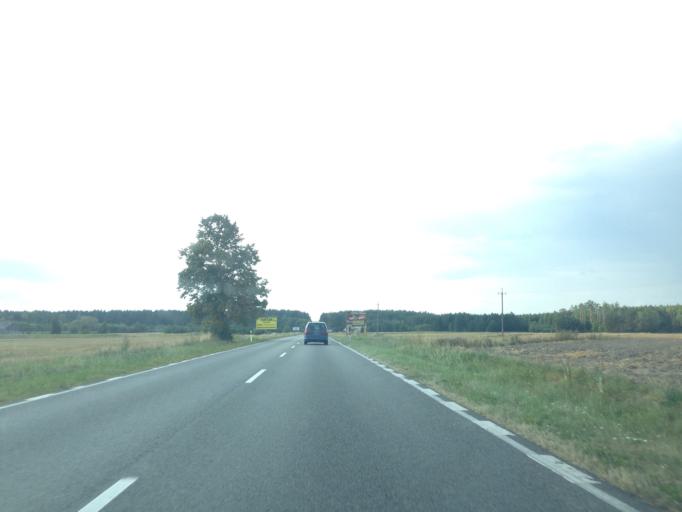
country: PL
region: Kujawsko-Pomorskie
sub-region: Powiat swiecki
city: Swiekatowo
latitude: 53.4783
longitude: 18.1441
